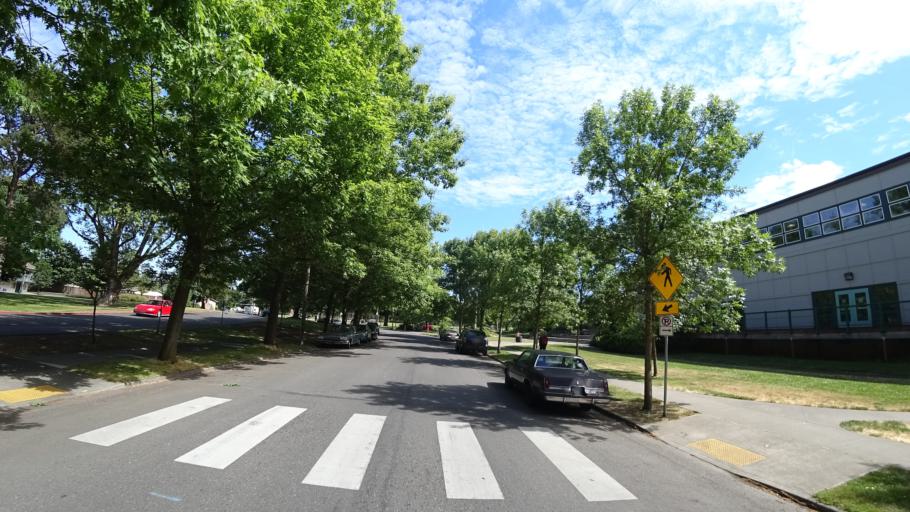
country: US
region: Washington
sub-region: Clark County
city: Vancouver
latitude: 45.5883
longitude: -122.7113
